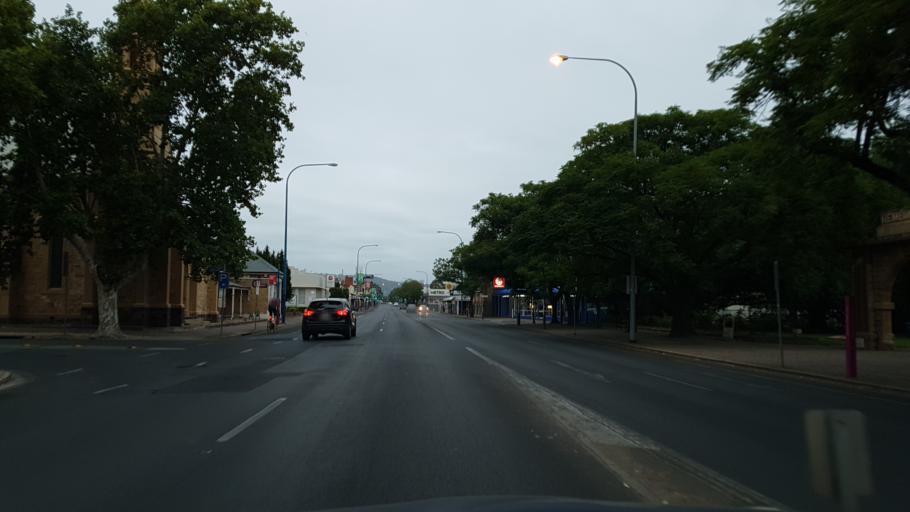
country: AU
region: South Australia
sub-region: Unley
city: Unley
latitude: -34.9514
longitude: 138.6076
